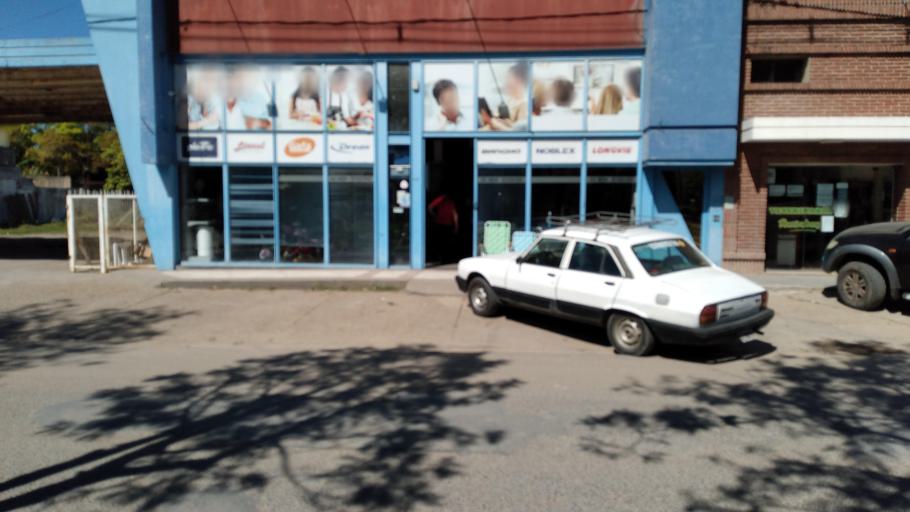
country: AR
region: Entre Rios
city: Villa Maria Grande
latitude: -31.6628
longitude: -59.9046
